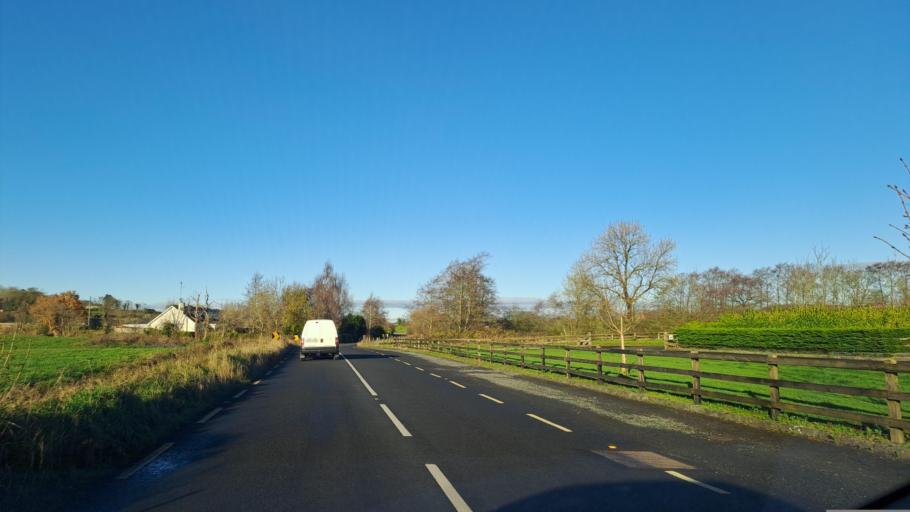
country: IE
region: Ulster
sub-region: An Cabhan
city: Mullagh
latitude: 53.8272
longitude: -6.9519
